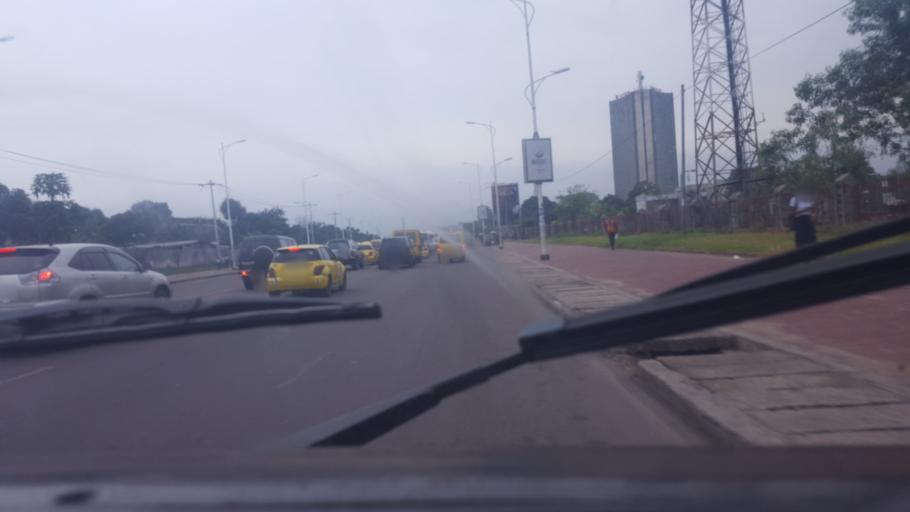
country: CD
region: Kinshasa
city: Kinshasa
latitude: -4.3327
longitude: 15.2965
